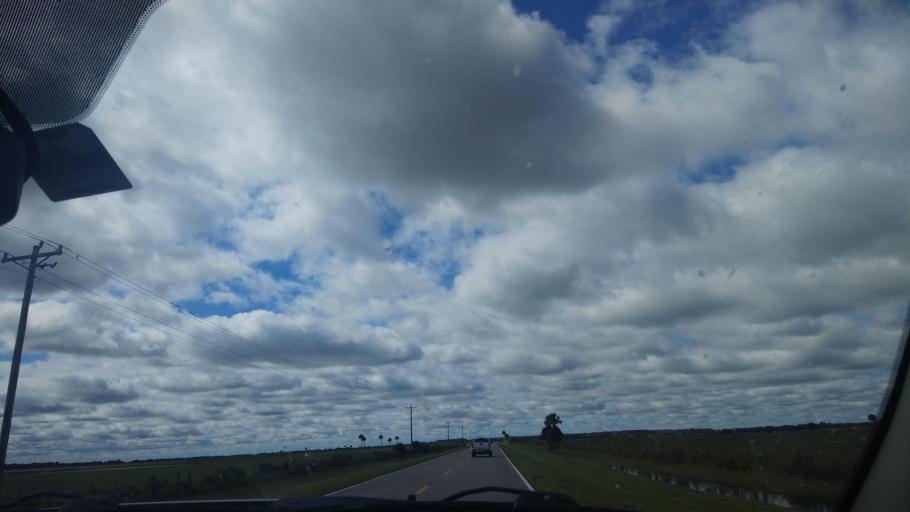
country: US
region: Florida
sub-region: Okeechobee County
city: Okeechobee
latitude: 27.3907
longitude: -80.9316
